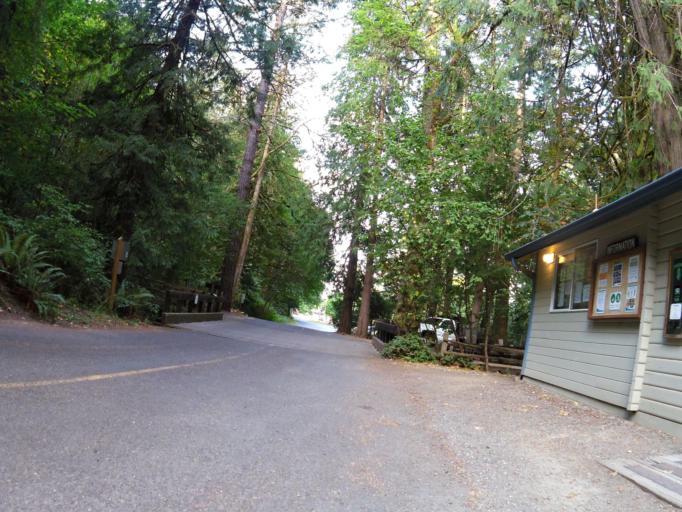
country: US
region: Washington
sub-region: Mason County
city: Allyn
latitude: 47.3778
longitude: -122.9731
